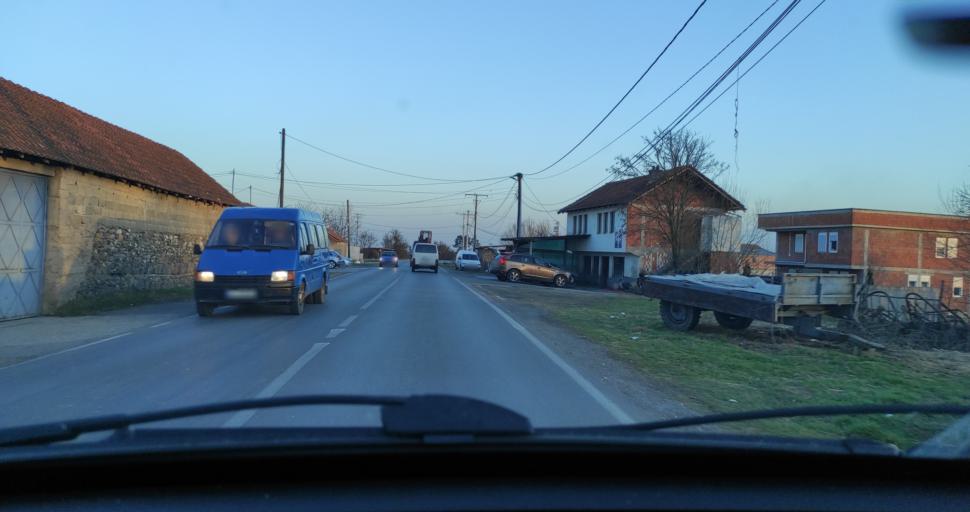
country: XK
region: Gjakova
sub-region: Komuna e Gjakoves
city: Gjakove
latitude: 42.4288
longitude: 20.3859
